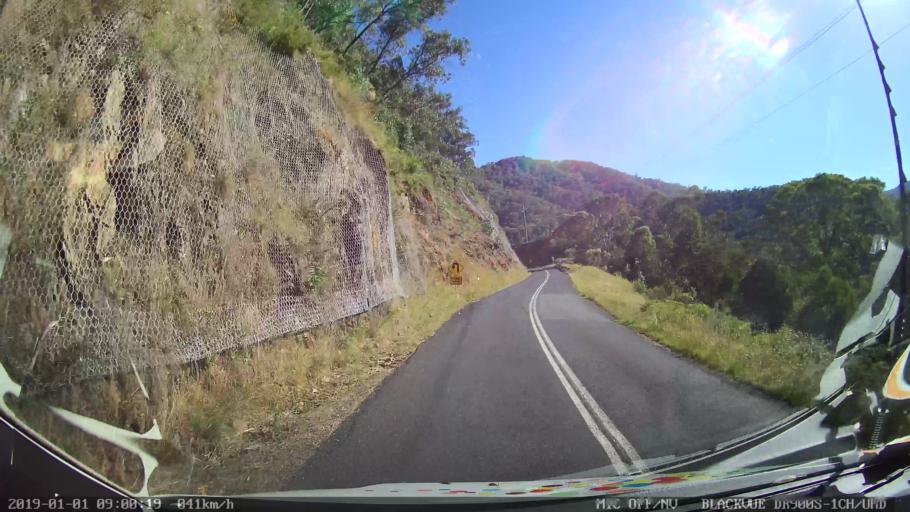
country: AU
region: New South Wales
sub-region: Snowy River
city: Jindabyne
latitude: -36.2361
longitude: 148.1819
